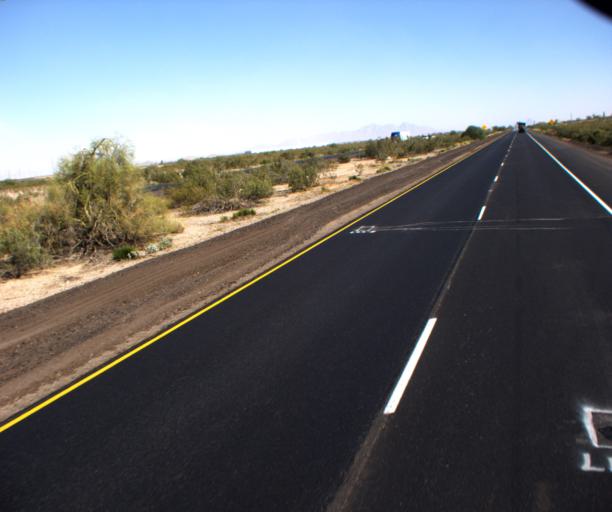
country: US
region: Arizona
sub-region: Pinal County
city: Casa Grande
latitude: 32.8302
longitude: -111.7053
